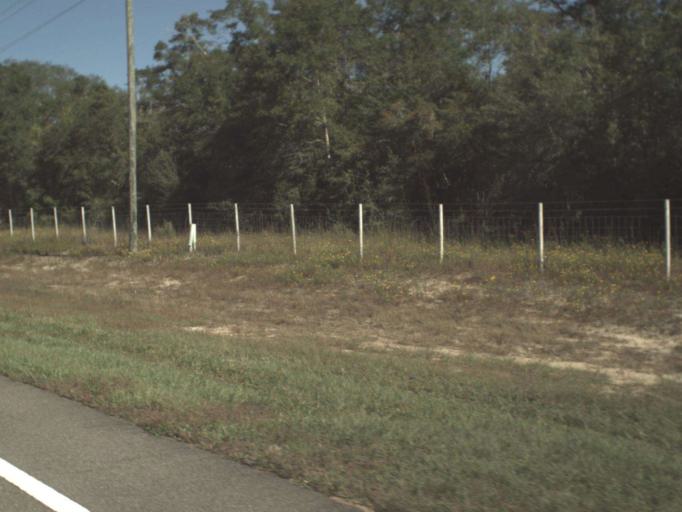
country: US
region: Florida
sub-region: Walton County
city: Freeport
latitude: 30.5844
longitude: -85.9361
